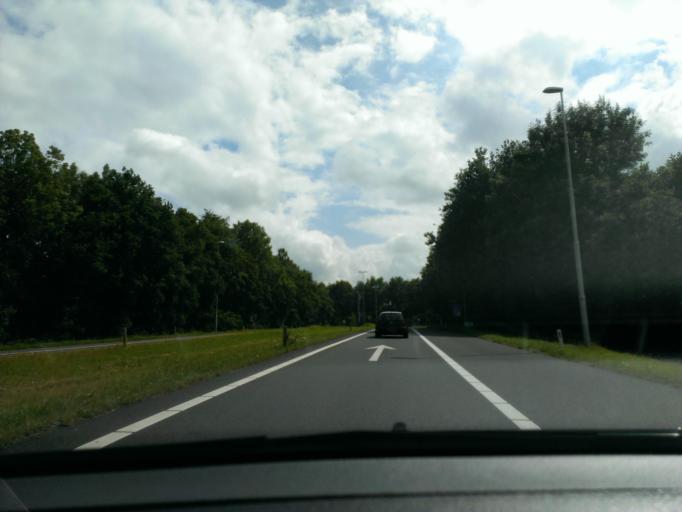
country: NL
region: Gelderland
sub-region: Gemeente Epe
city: Epe
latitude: 52.3353
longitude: 6.0127
